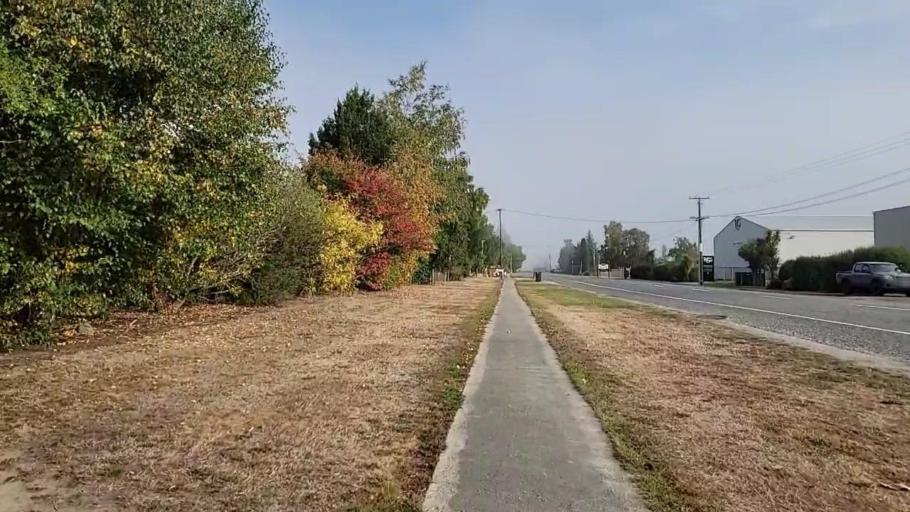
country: NZ
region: Southland
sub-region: Gore District
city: Gore
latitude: -45.6360
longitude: 169.3659
